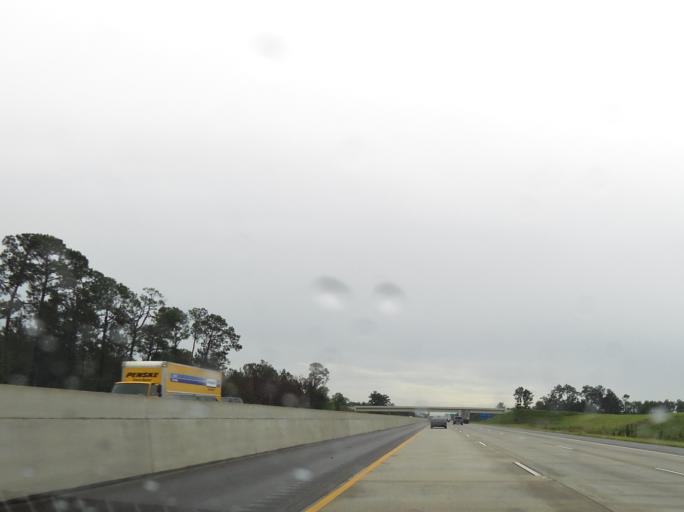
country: US
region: Georgia
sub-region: Cook County
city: Sparks
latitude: 31.2391
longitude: -83.4652
